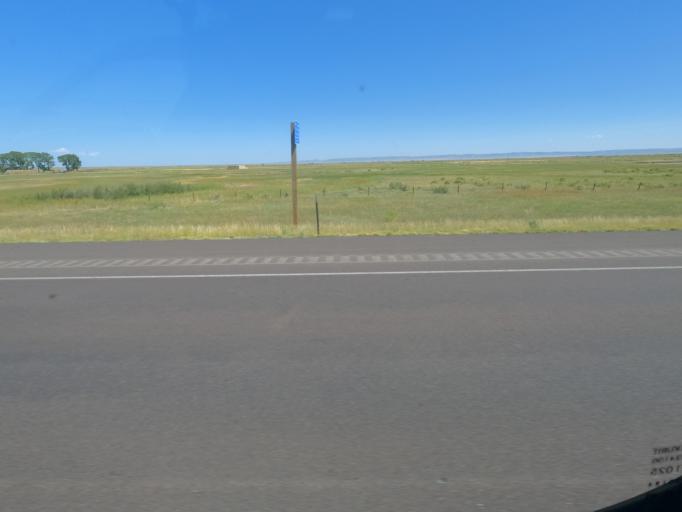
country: US
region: Wyoming
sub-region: Albany County
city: Laramie
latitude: 41.4037
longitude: -105.8312
